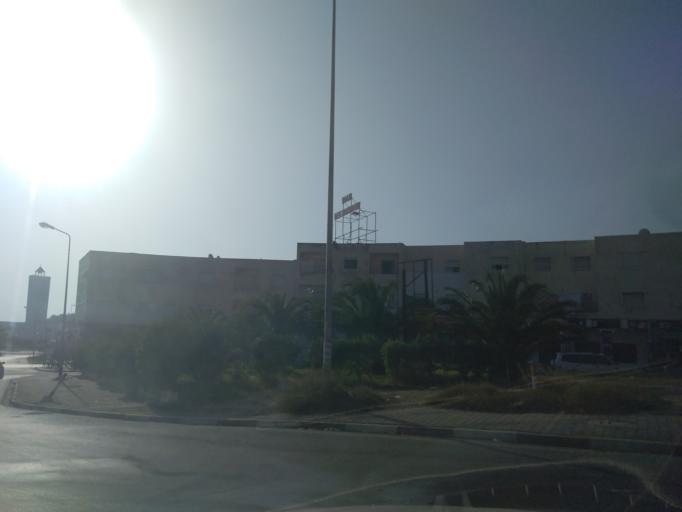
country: TN
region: Manouba
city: Manouba
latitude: 36.7856
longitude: 10.0807
